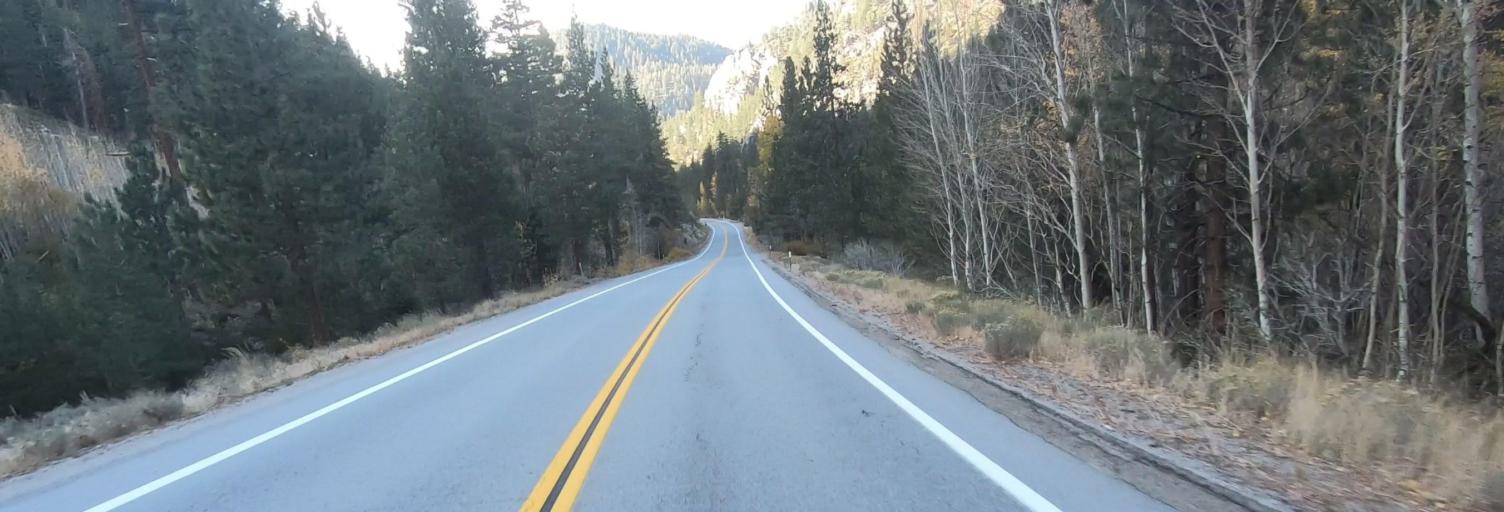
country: US
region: Nevada
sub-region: Douglas County
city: Gardnerville Ranchos
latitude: 38.7684
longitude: -119.8714
